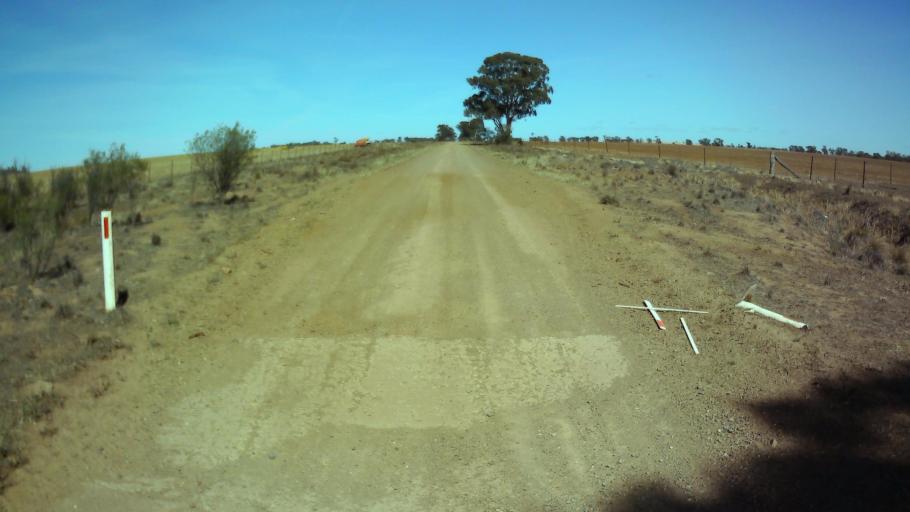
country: AU
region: New South Wales
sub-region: Weddin
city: Grenfell
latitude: -33.7502
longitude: 147.8948
